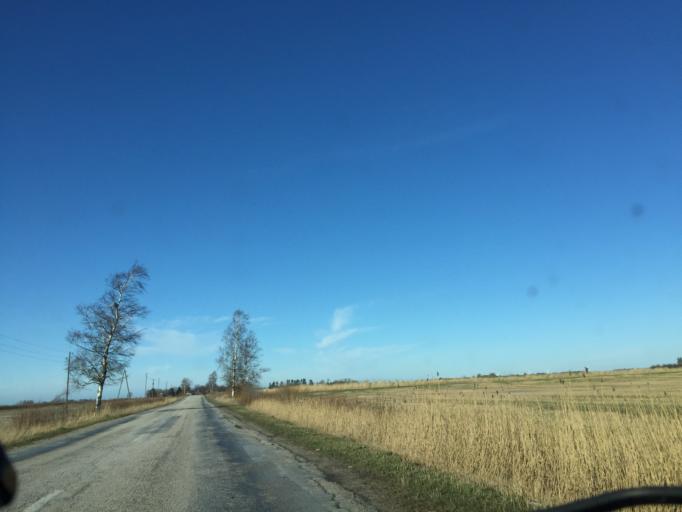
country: LV
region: Ventspils Rajons
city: Piltene
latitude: 57.3064
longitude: 21.6431
